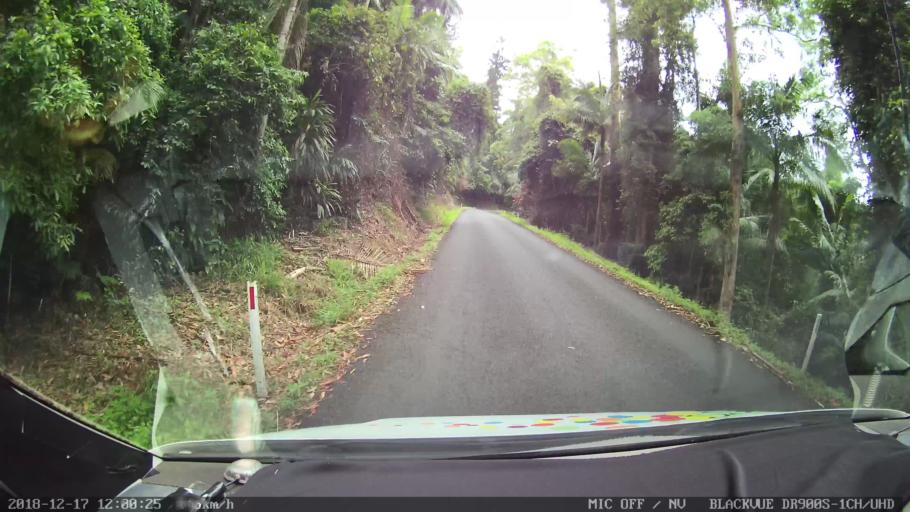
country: AU
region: New South Wales
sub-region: Kyogle
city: Kyogle
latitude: -28.5256
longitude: 152.5677
